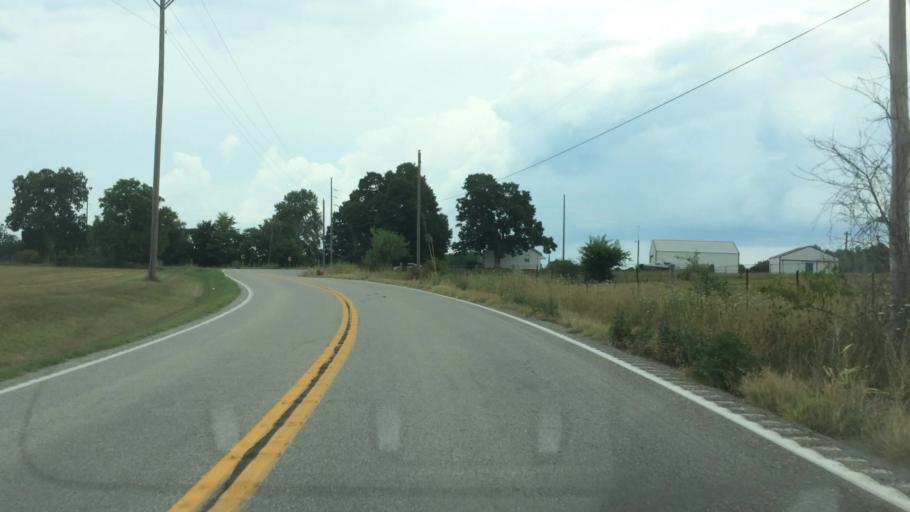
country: US
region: Missouri
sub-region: Greene County
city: Strafford
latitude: 37.2520
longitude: -93.1353
